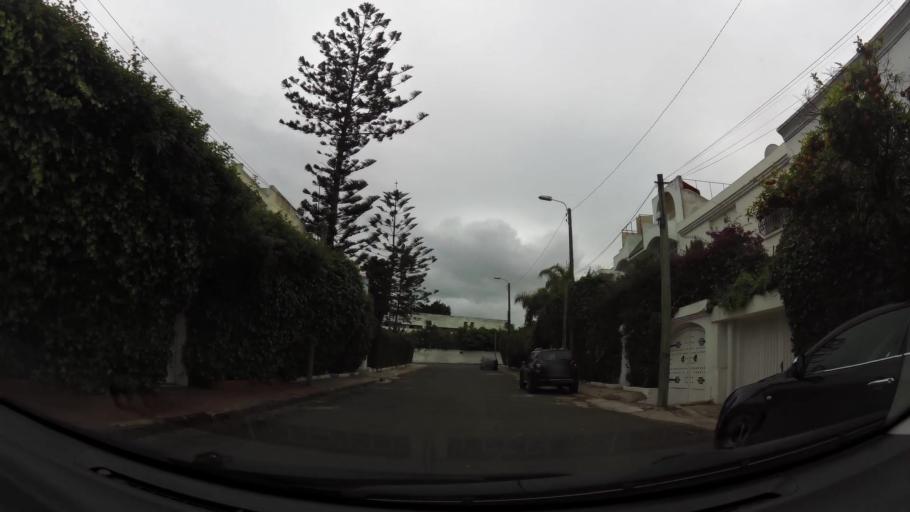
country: MA
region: Grand Casablanca
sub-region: Casablanca
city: Casablanca
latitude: 33.5938
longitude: -7.6473
